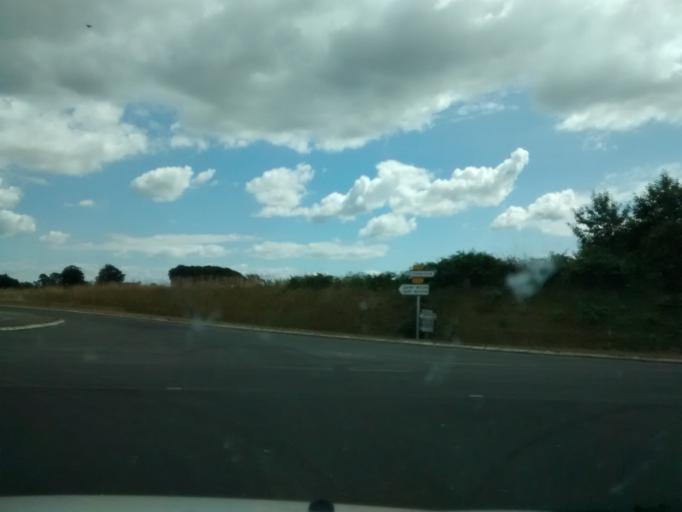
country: FR
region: Brittany
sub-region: Departement du Finistere
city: Lesneven
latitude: 48.5734
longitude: -4.2745
